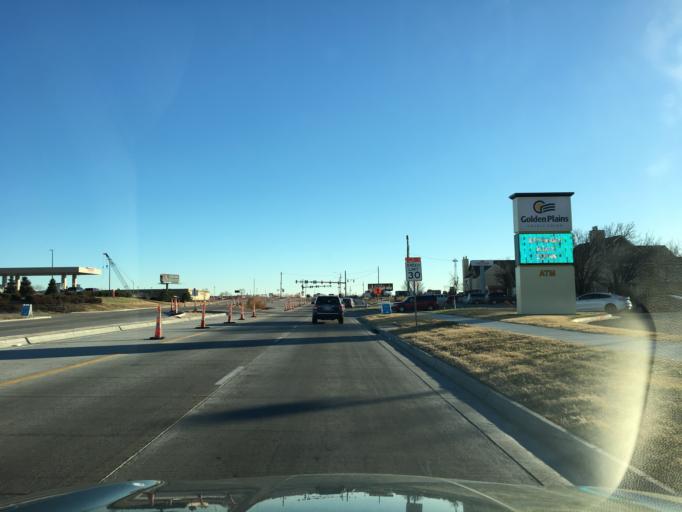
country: US
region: Kansas
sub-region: Sedgwick County
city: Bellaire
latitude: 37.6817
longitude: -97.2263
